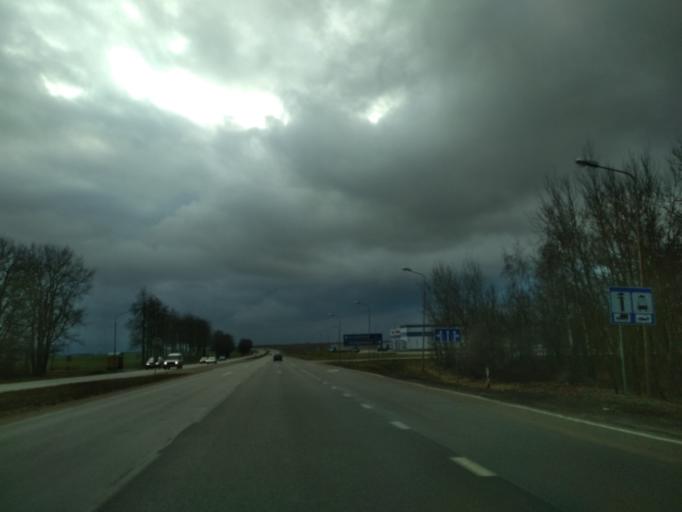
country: BY
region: Minsk
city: Luhavaya Slabada
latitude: 53.7591
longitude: 27.8297
